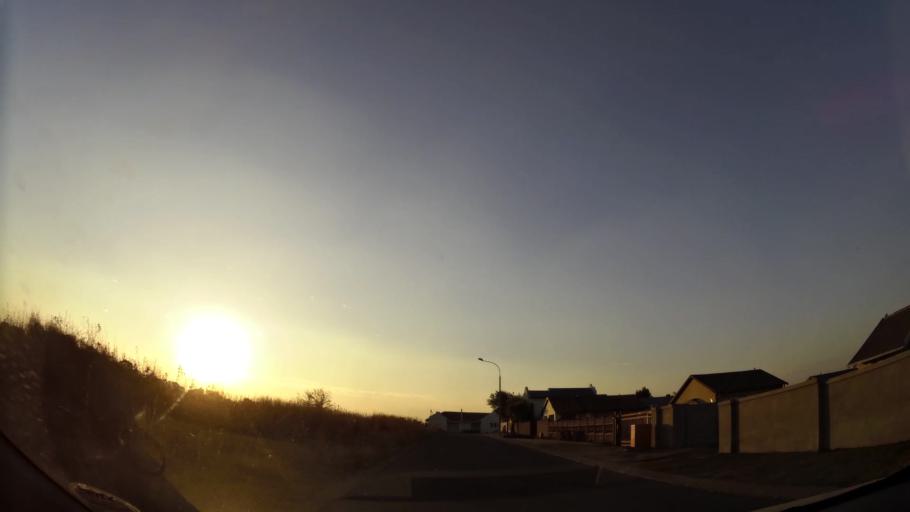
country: ZA
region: Gauteng
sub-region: West Rand District Municipality
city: Randfontein
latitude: -26.2079
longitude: 27.7047
